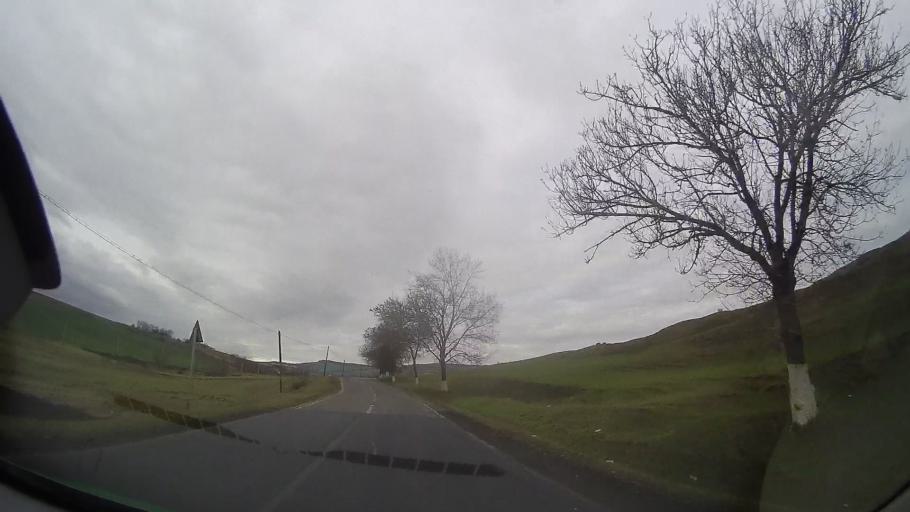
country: RO
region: Bistrita-Nasaud
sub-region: Comuna Urmenis
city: Urmenis
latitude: 46.7615
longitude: 24.3822
